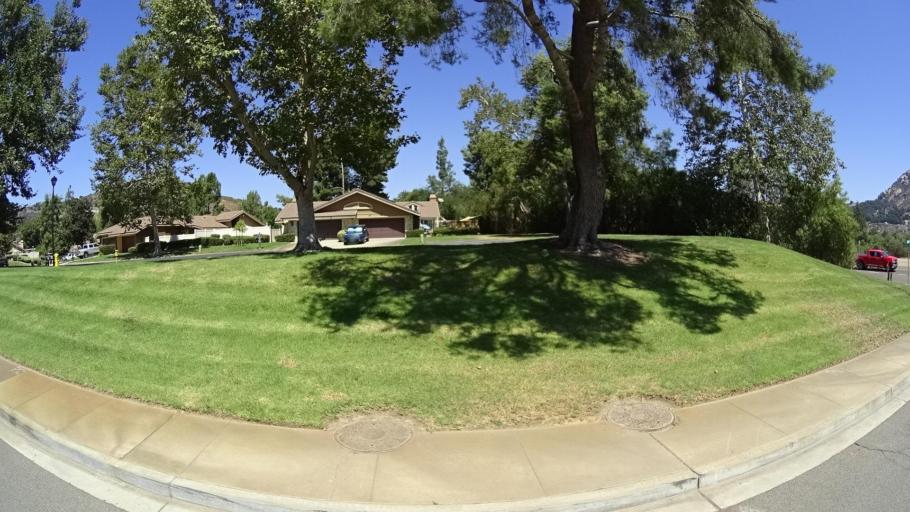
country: US
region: California
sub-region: San Diego County
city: Rainbow
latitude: 33.3413
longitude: -117.1605
